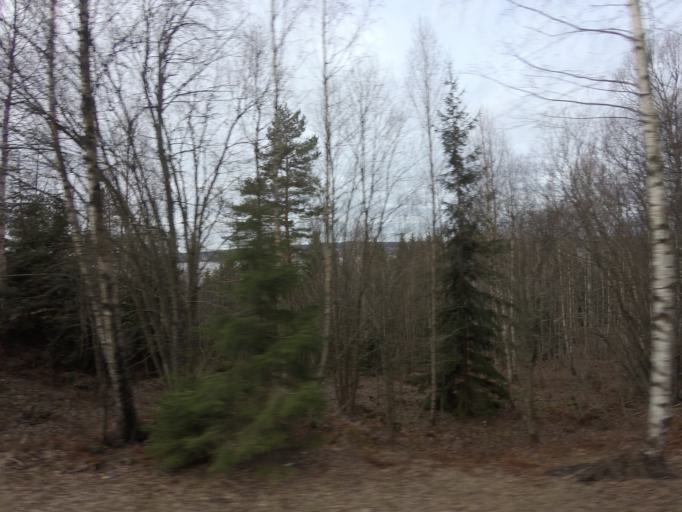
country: NO
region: Akershus
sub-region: Enebakk
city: Flateby
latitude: 59.8162
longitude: 11.2460
